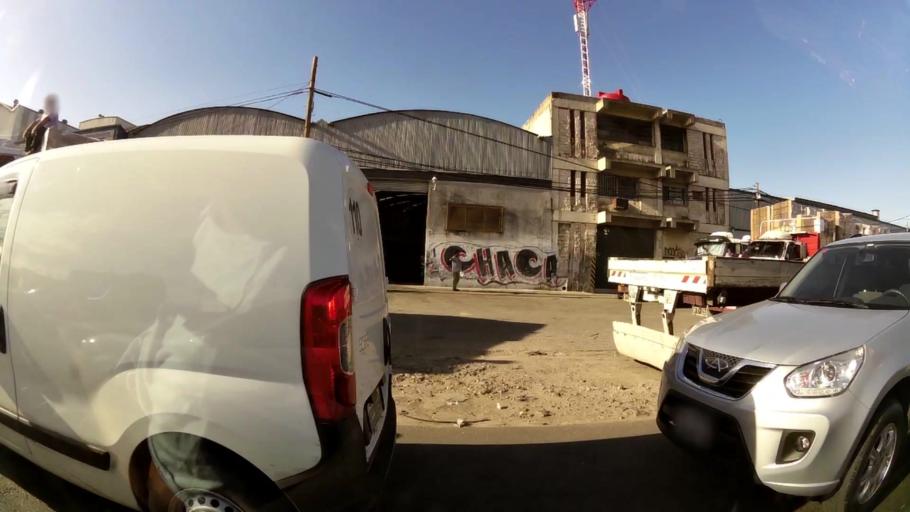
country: AR
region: Buenos Aires
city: Hurlingham
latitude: -34.5628
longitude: -58.6145
